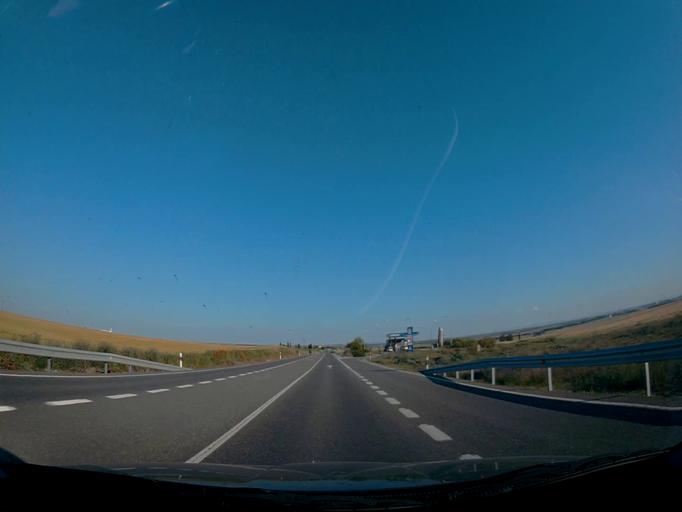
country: ES
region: Castille-La Mancha
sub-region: Province of Toledo
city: Maqueda
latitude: 40.0798
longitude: -4.3802
